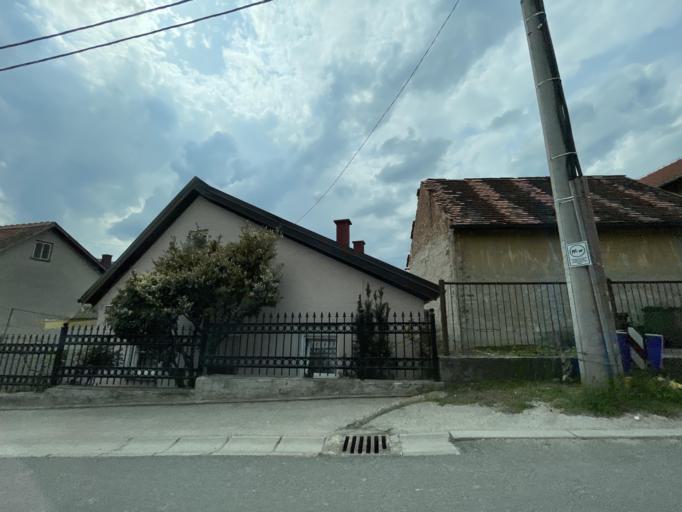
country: HR
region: Grad Zagreb
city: Zagreb
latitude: 45.8515
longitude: 15.9497
